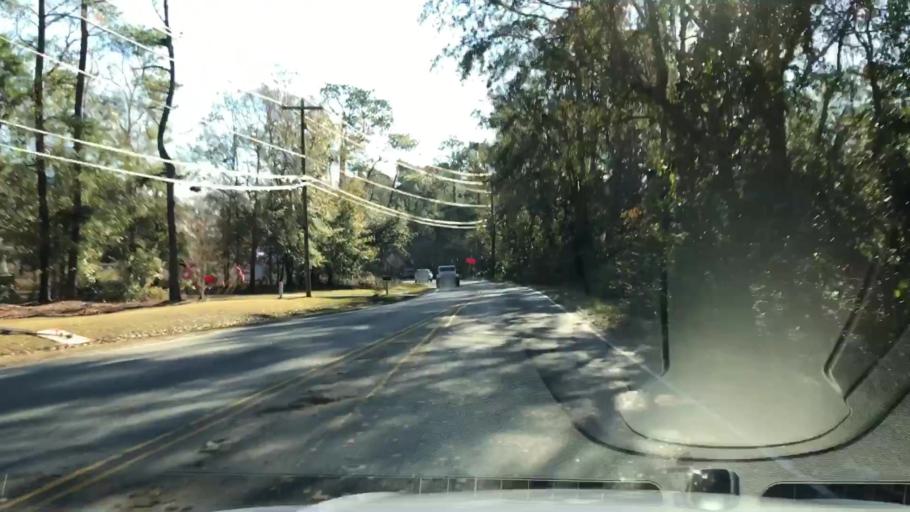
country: US
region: South Carolina
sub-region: Charleston County
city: Lincolnville
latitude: 32.9824
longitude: -80.1402
